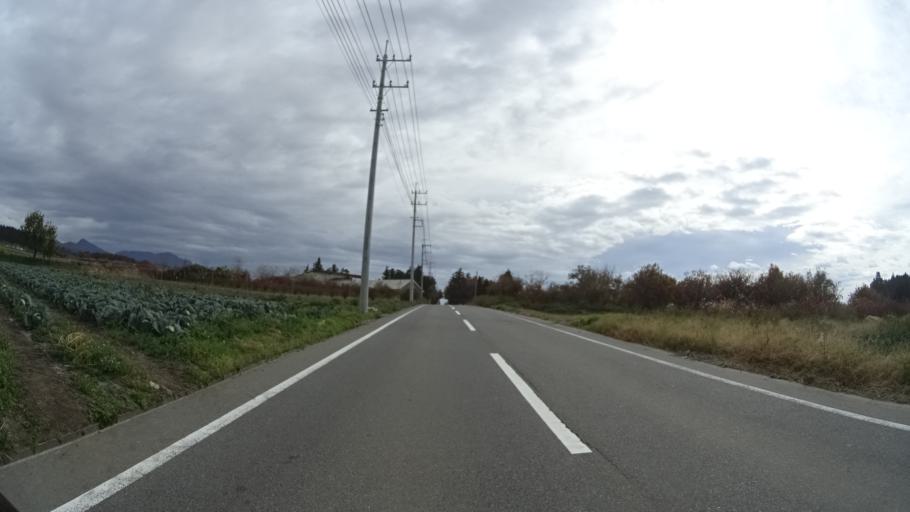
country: JP
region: Gunma
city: Shibukawa
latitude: 36.5271
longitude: 139.0634
